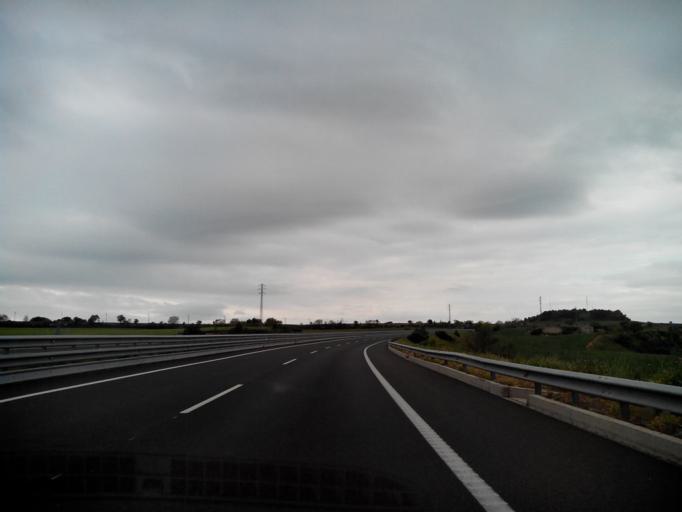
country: ES
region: Catalonia
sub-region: Provincia de Lleida
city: Cervera
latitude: 41.6858
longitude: 1.3044
